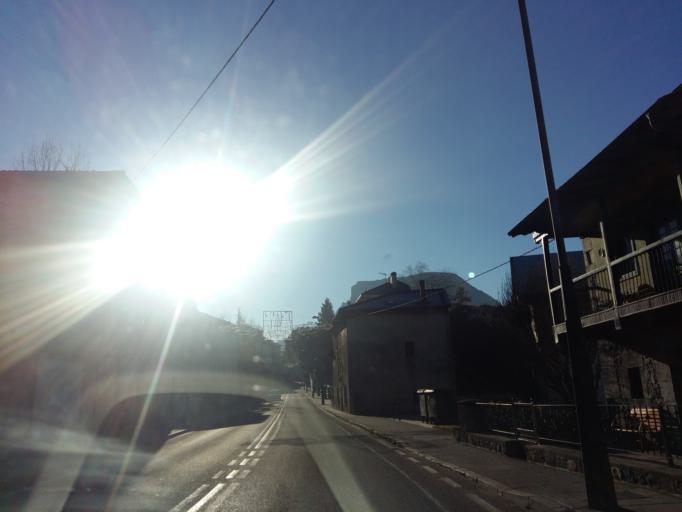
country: ES
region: Cantabria
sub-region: Provincia de Cantabria
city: Ramales de la Victoria
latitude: 43.2605
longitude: -3.4663
